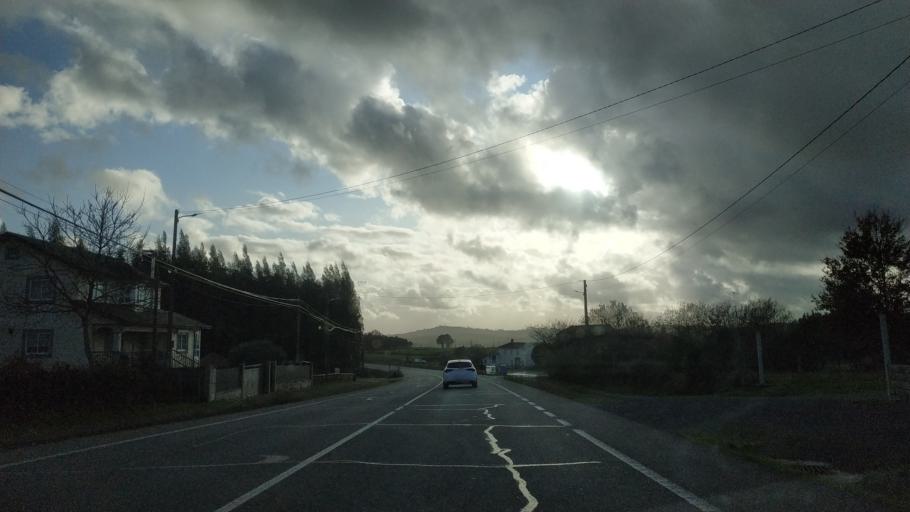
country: ES
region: Galicia
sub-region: Provincia da Coruna
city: Arzua
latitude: 42.9126
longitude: -8.1708
